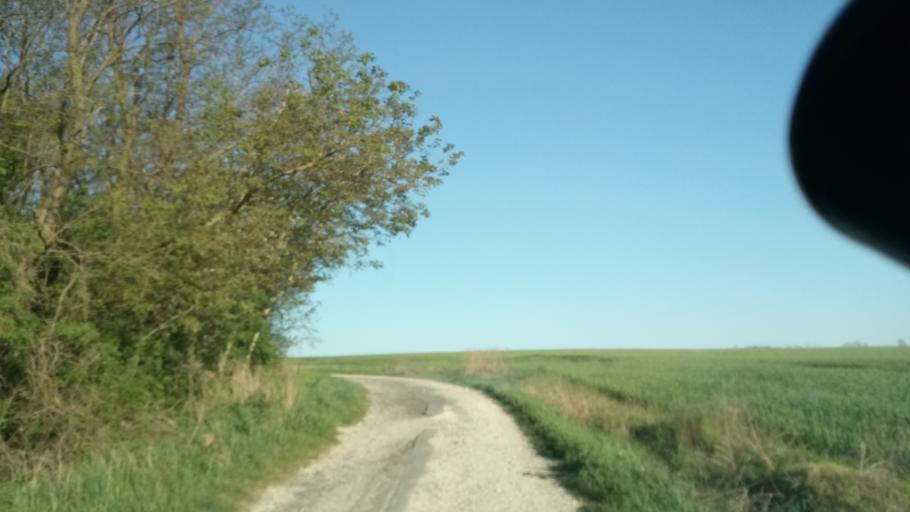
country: HU
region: Zala
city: Sarmellek
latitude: 46.7043
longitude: 17.1000
